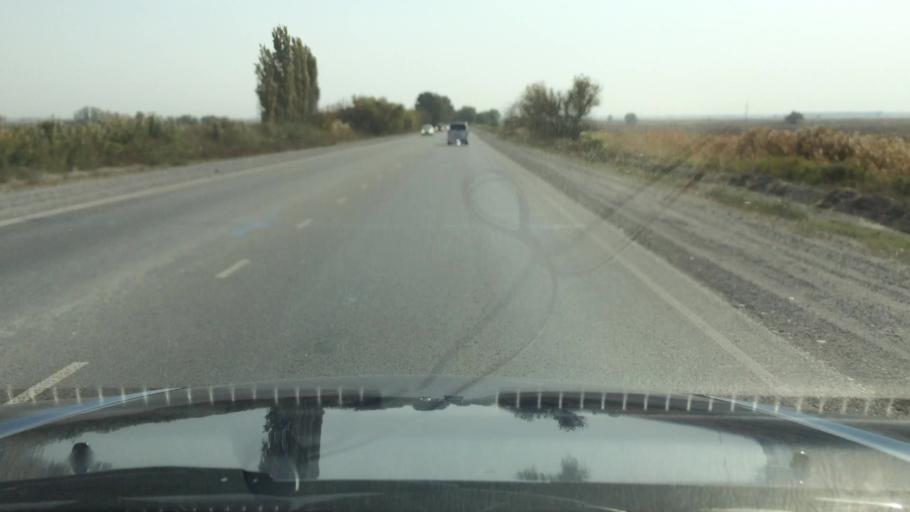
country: KG
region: Chuy
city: Lebedinovka
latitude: 42.9255
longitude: 74.7004
